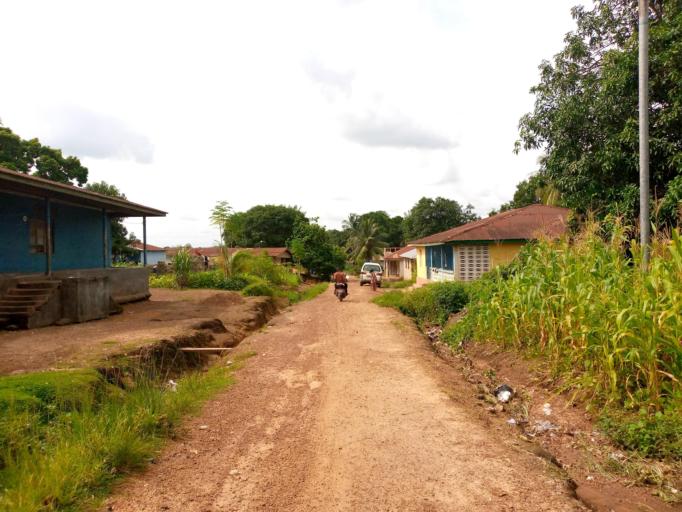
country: SL
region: Northern Province
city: Magburaka
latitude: 8.7236
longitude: -11.9400
